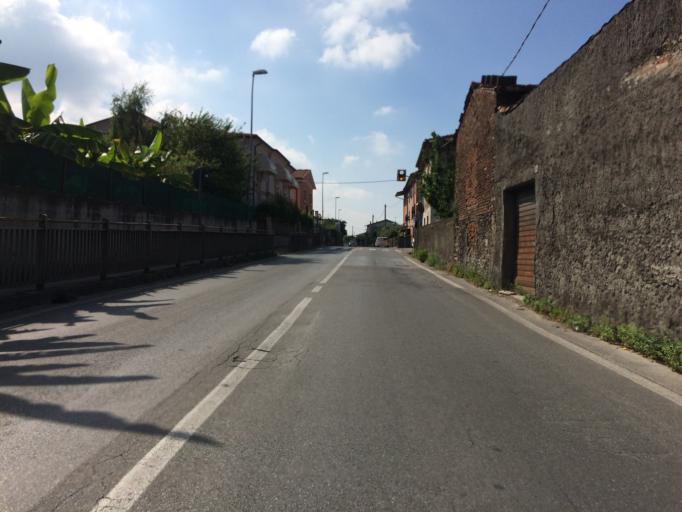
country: IT
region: Tuscany
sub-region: Provincia di Massa-Carrara
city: San Vito-Cerreto
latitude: 44.0209
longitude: 10.1492
